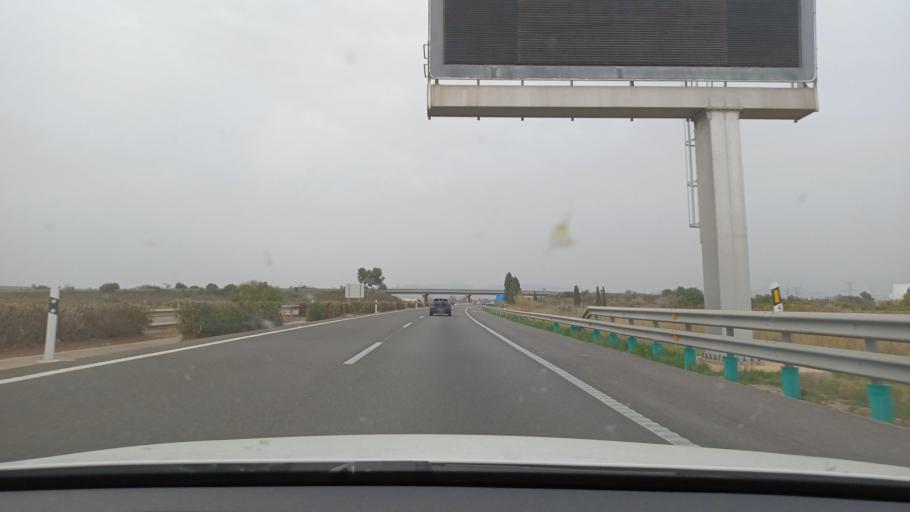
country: ES
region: Valencia
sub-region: Provincia de Castello
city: Vila-real
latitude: 39.9420
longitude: -0.1334
